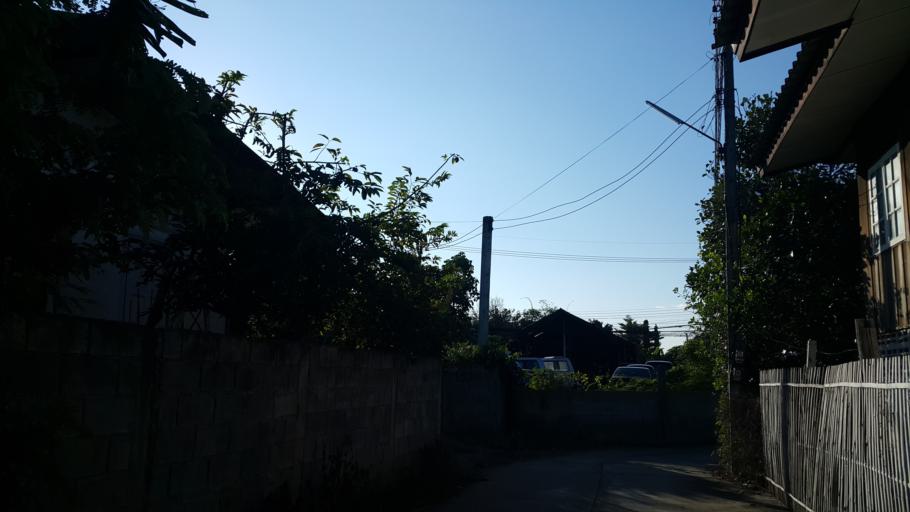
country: TH
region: Chiang Mai
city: Saraphi
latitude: 18.7483
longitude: 99.0483
